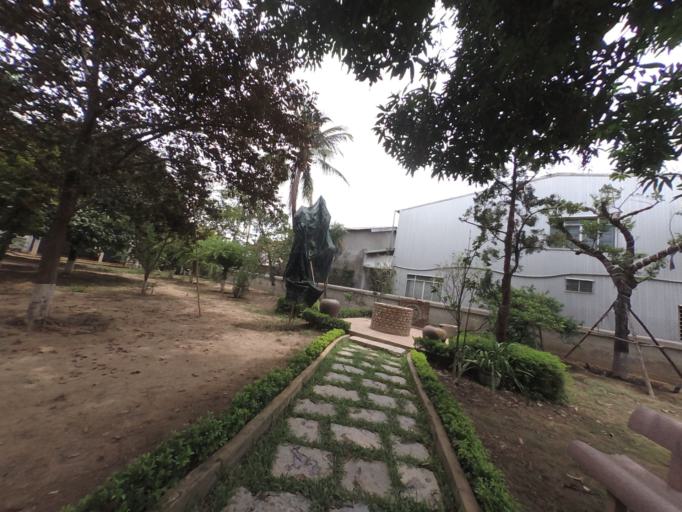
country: VN
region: Thua Thien-Hue
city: Hue
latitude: 16.4554
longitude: 107.5538
